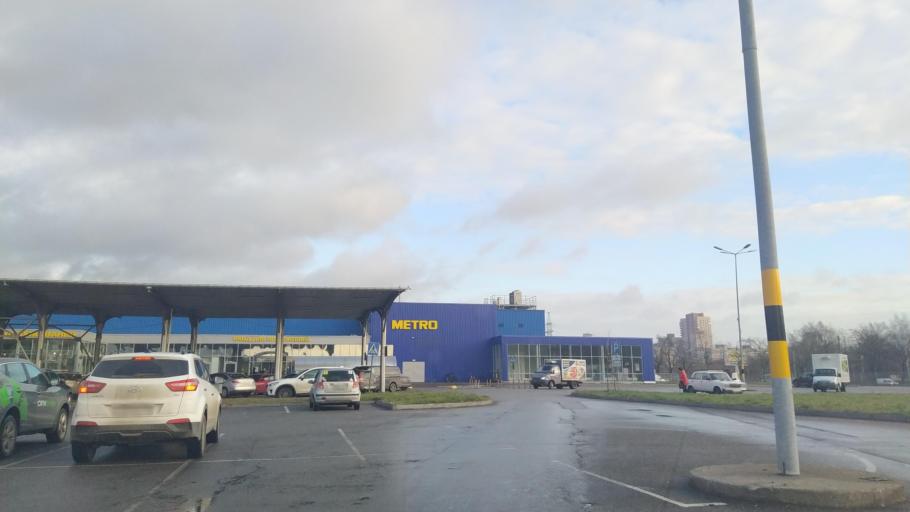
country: RU
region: St.-Petersburg
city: Krasnogvargeisky
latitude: 59.9401
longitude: 30.4546
